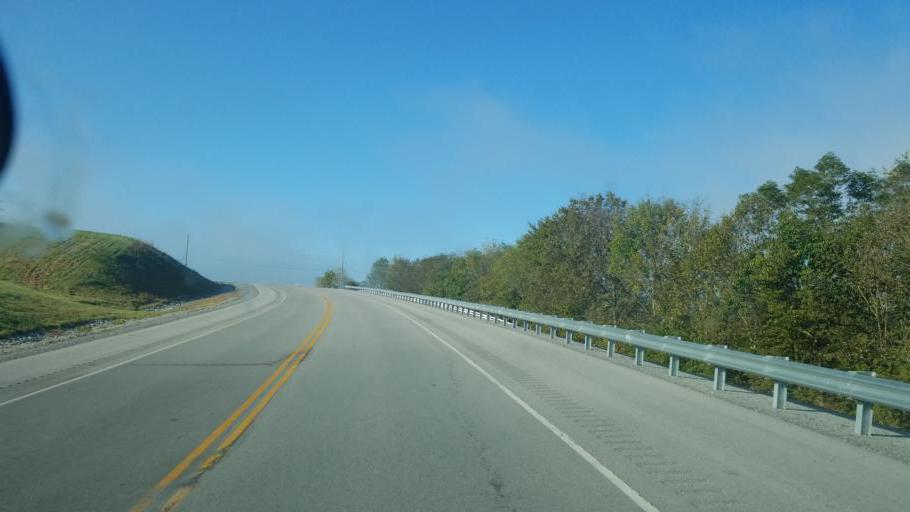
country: US
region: Kentucky
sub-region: Fleming County
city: Flemingsburg
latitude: 38.4392
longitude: -83.7088
